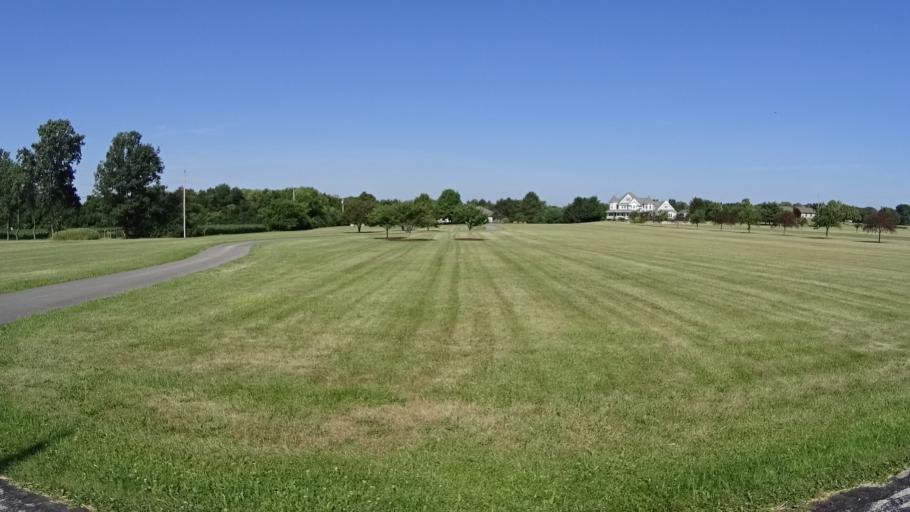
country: US
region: Ohio
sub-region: Huron County
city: Bellevue
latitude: 41.3648
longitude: -82.8189
